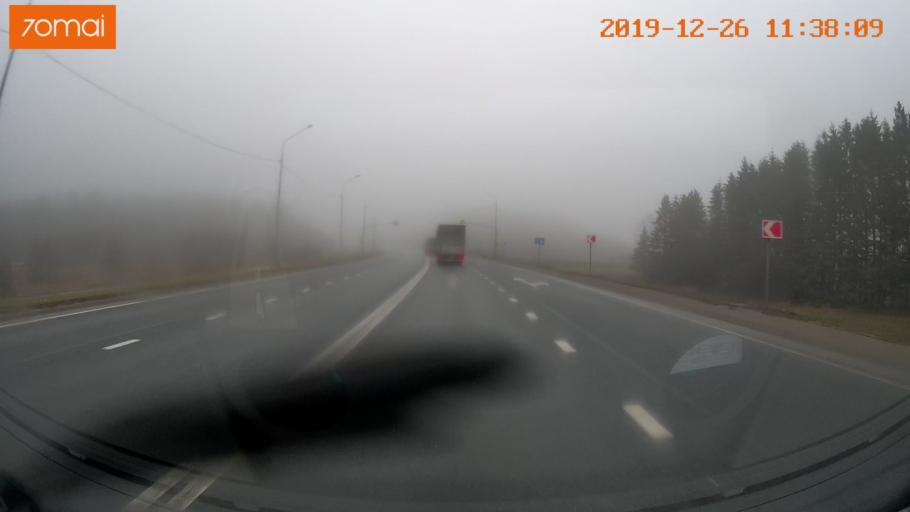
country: RU
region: Vologda
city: Sheksna
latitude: 59.2086
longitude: 38.6247
